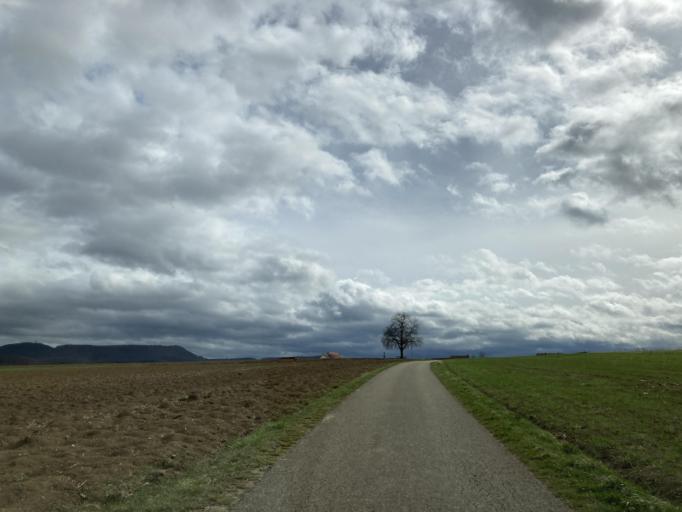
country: DE
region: Baden-Wuerttemberg
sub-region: Tuebingen Region
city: Gomaringen
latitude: 48.4670
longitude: 9.0998
